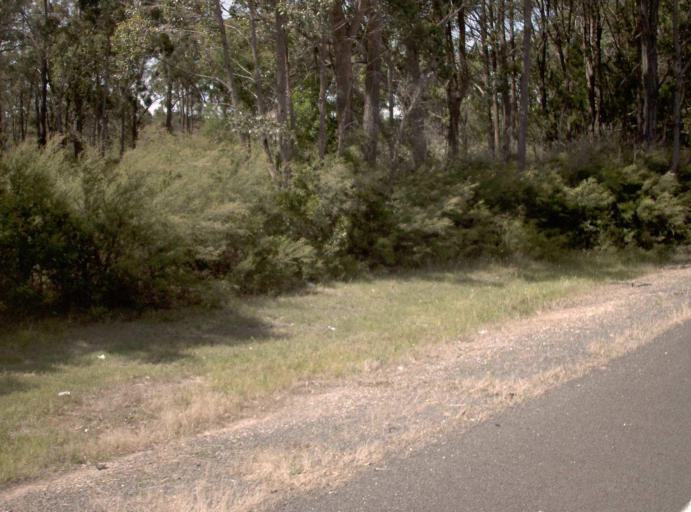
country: AU
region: Victoria
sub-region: East Gippsland
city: Bairnsdale
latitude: -37.9112
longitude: 147.3128
